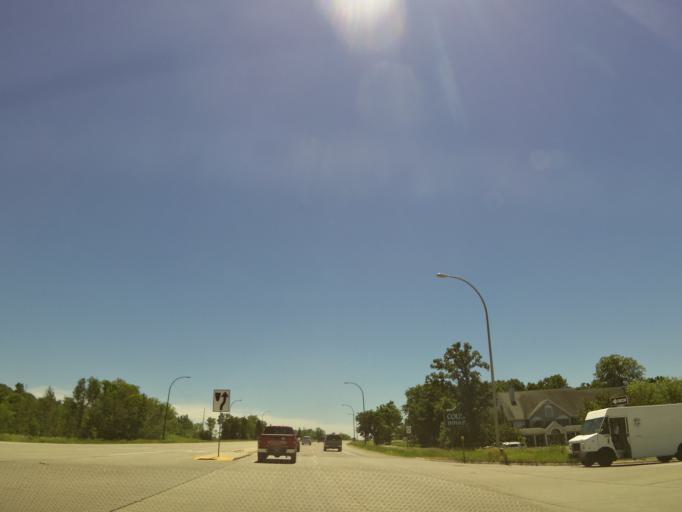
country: US
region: Minnesota
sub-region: Becker County
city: Detroit Lakes
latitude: 46.7998
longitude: -95.8081
